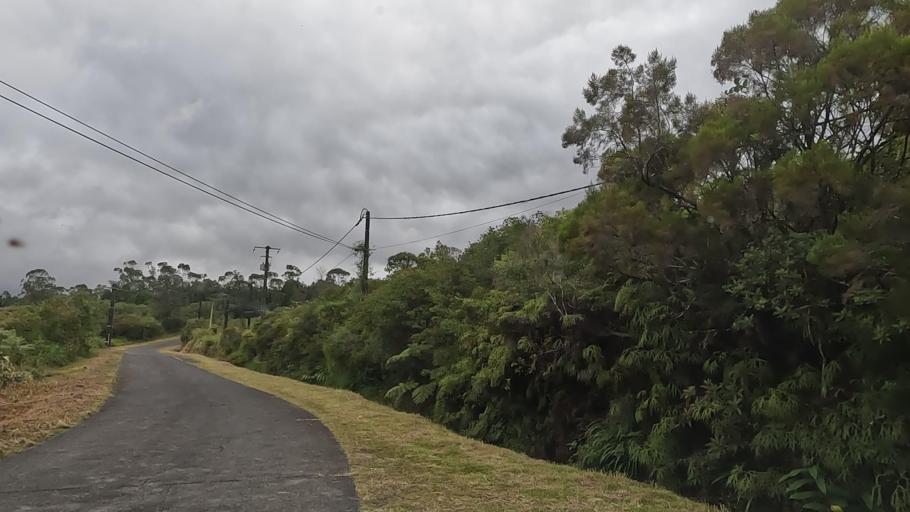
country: RE
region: Reunion
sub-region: Reunion
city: Saint-Benoit
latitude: -21.1210
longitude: 55.6363
